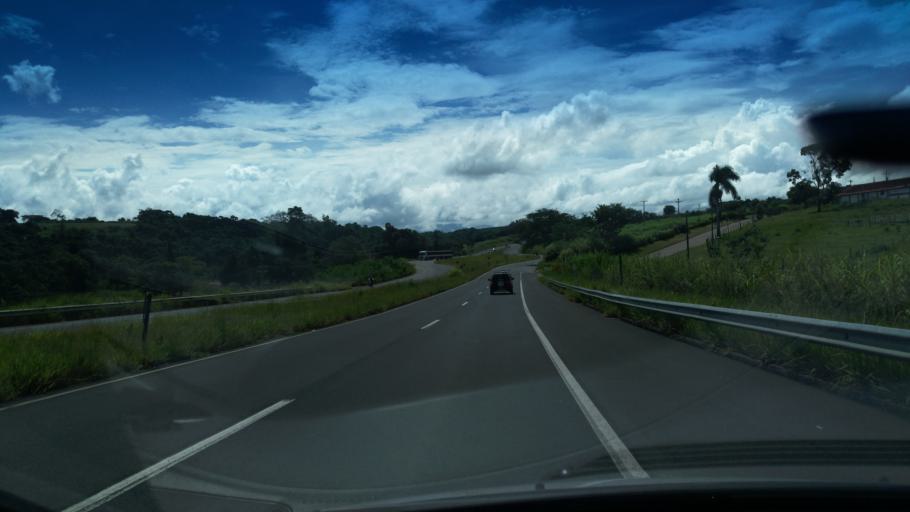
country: BR
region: Sao Paulo
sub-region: Santo Antonio Do Jardim
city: Espirito Santo do Pinhal
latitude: -22.1669
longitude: -46.7389
